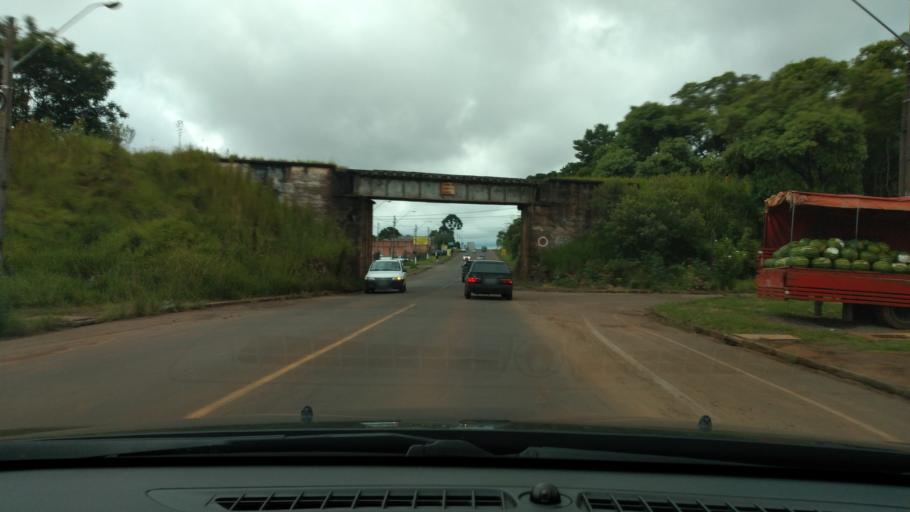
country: BR
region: Parana
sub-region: Guarapuava
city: Guarapuava
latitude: -25.3940
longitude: -51.4854
